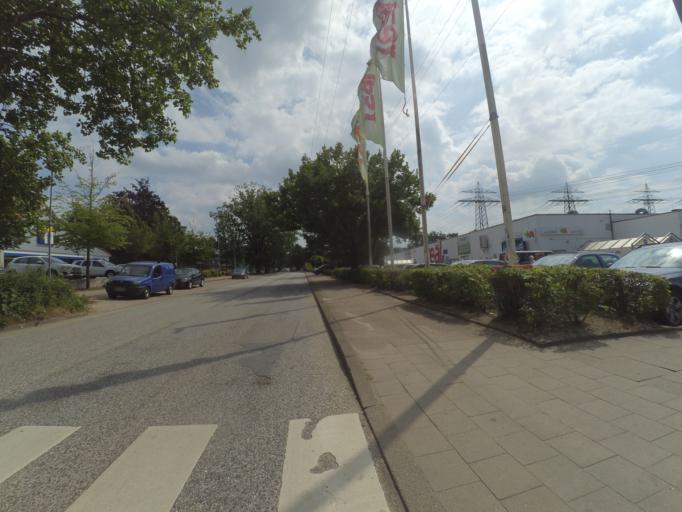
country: DE
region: Hamburg
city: Eidelstedt
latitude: 53.5848
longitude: 9.8722
